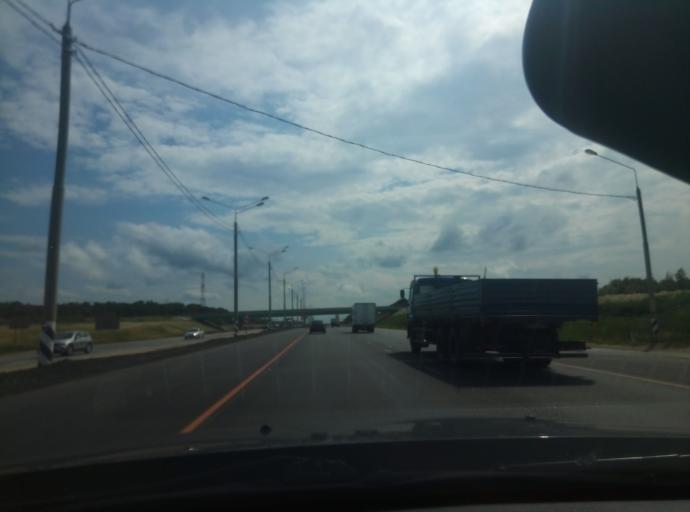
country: RU
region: Tula
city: Novogurovskiy
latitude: 54.4726
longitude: 37.5116
